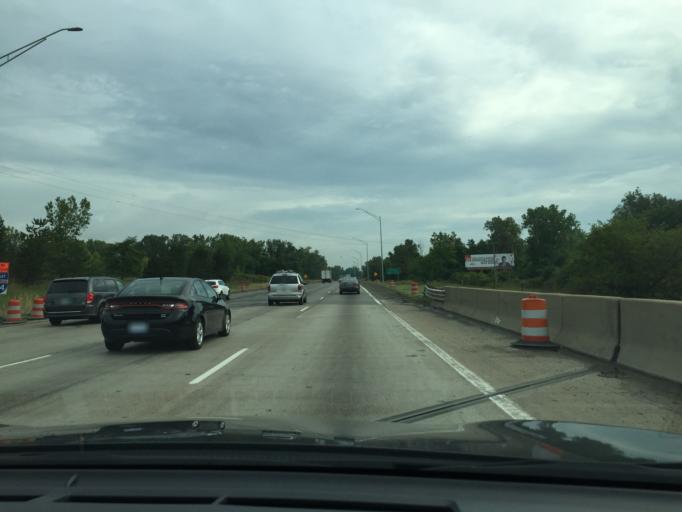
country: US
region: Michigan
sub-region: Wayne County
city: Taylor
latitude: 42.2542
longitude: -83.2983
